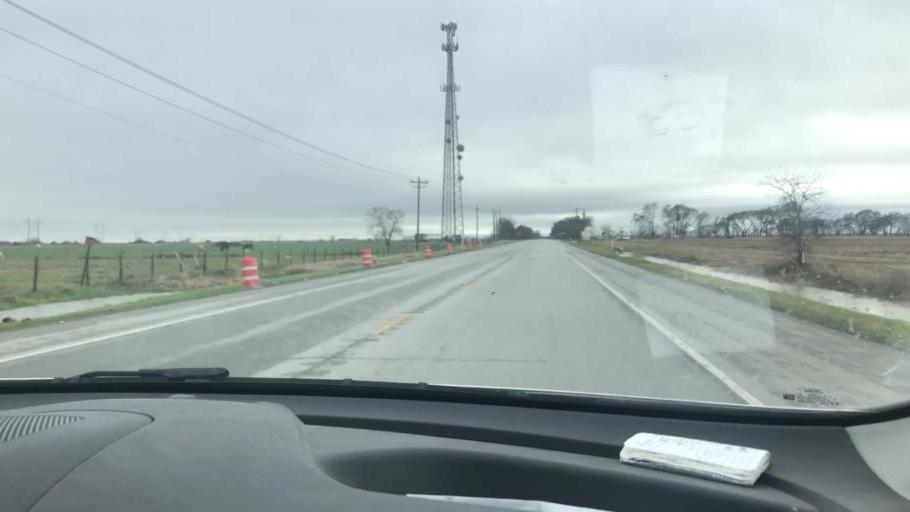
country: US
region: Texas
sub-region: Wharton County
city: Boling
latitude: 29.1392
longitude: -95.9848
